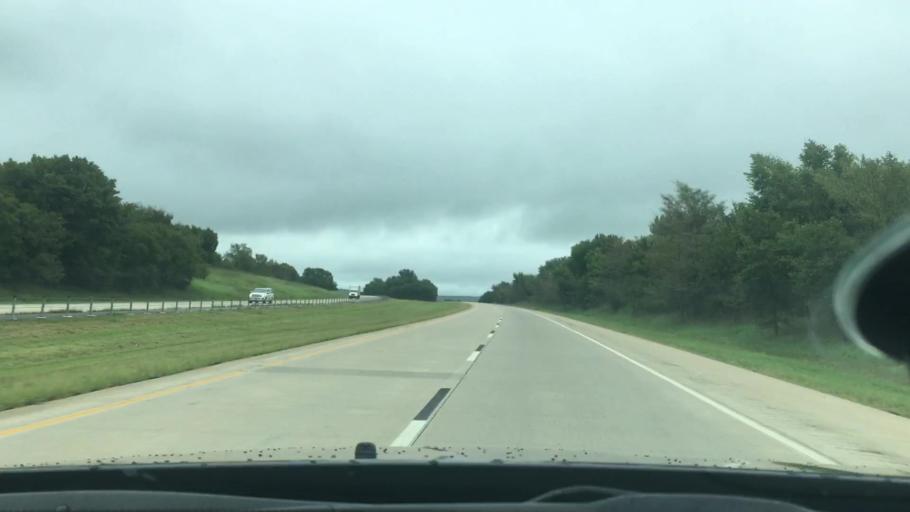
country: US
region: Oklahoma
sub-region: Okmulgee County
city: Henryetta
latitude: 35.4294
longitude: -95.9072
